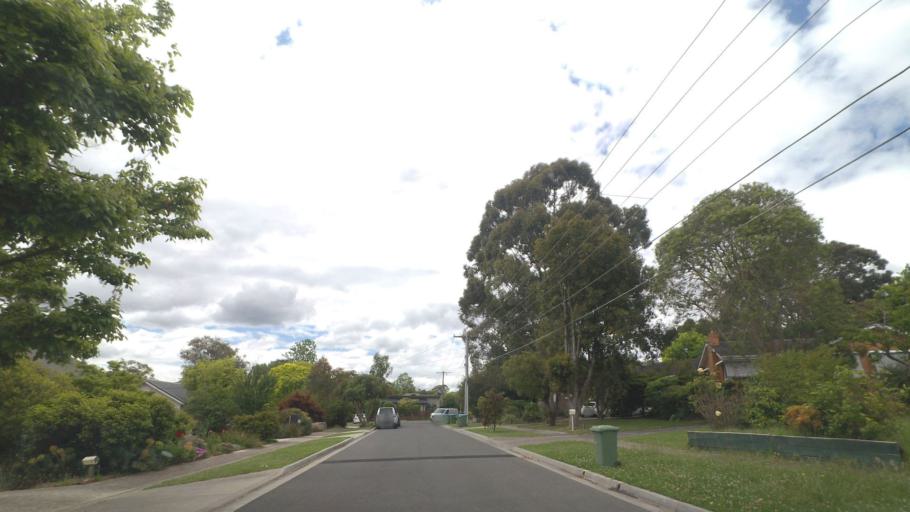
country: AU
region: Victoria
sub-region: Yarra Ranges
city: Kilsyth
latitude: -37.7973
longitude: 145.3056
